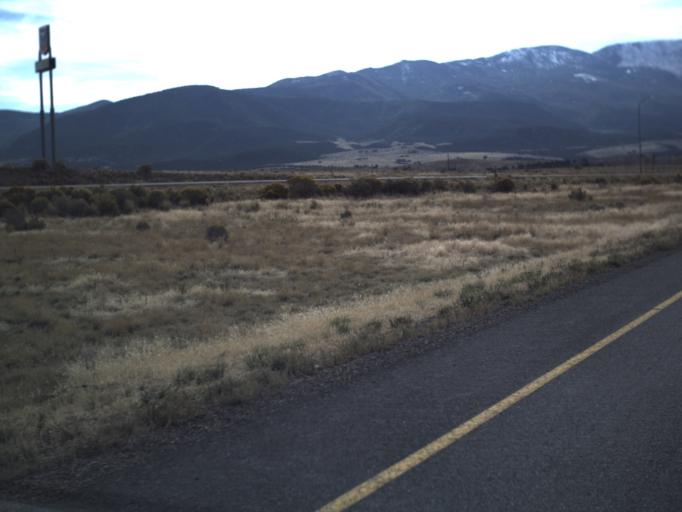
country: US
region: Utah
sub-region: Beaver County
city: Beaver
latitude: 38.6143
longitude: -112.6107
